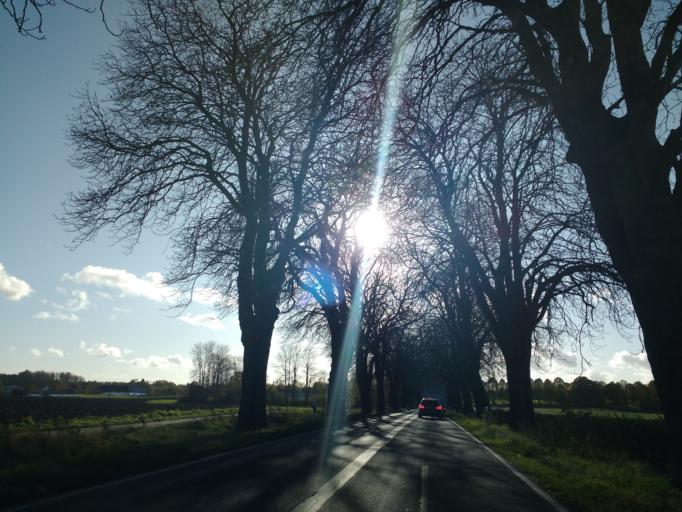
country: DE
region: Mecklenburg-Vorpommern
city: Klutz
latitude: 53.9353
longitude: 11.1551
